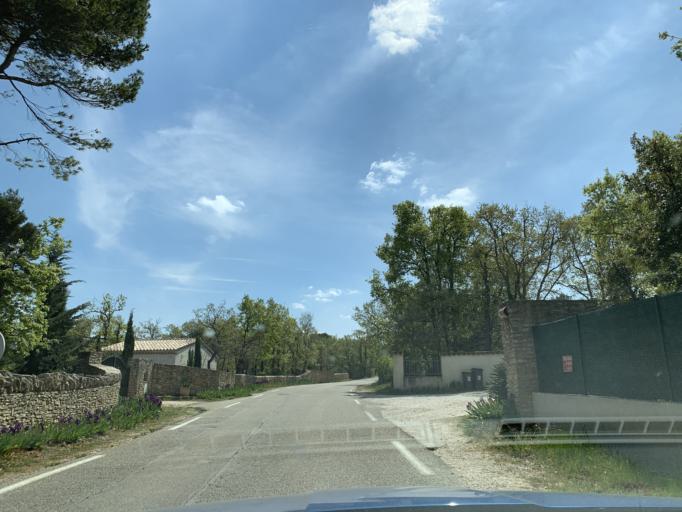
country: FR
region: Provence-Alpes-Cote d'Azur
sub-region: Departement du Vaucluse
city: Saint-Didier
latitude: 43.9758
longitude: 5.1131
